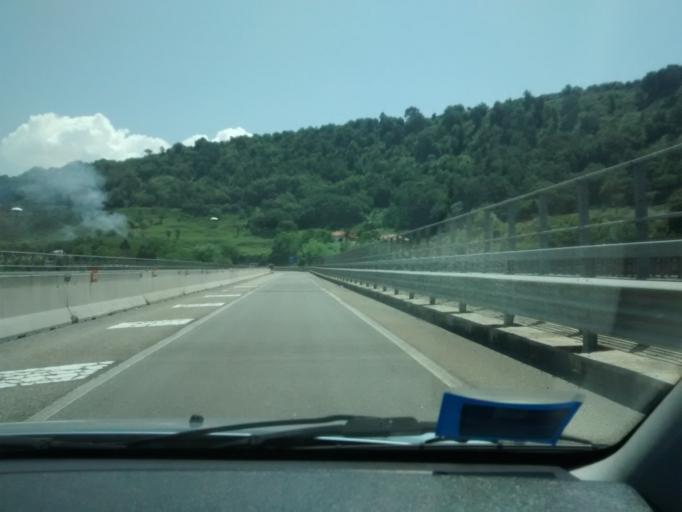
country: IT
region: Calabria
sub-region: Provincia di Catanzaro
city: Maida
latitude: 38.9026
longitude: 16.3857
